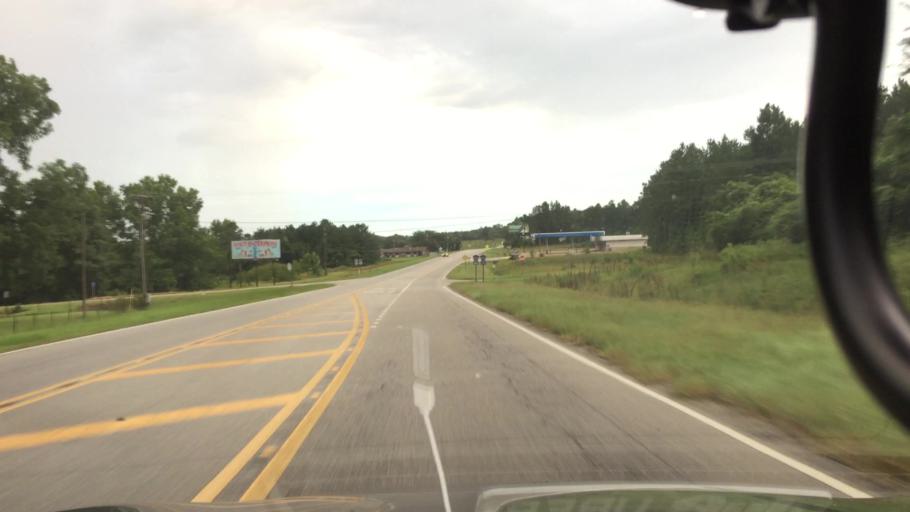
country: US
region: Alabama
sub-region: Pike County
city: Troy
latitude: 31.7110
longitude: -85.9590
